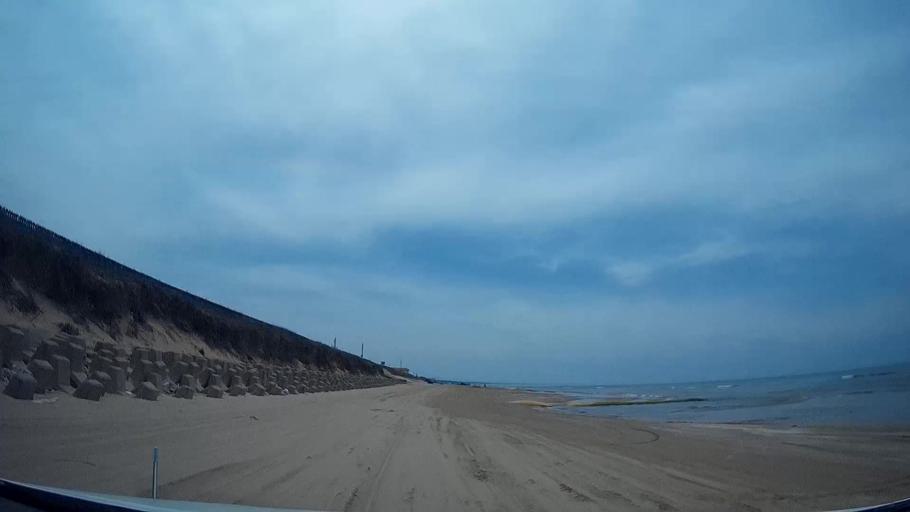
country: JP
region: Ishikawa
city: Hakui
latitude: 36.8990
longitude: 136.7671
